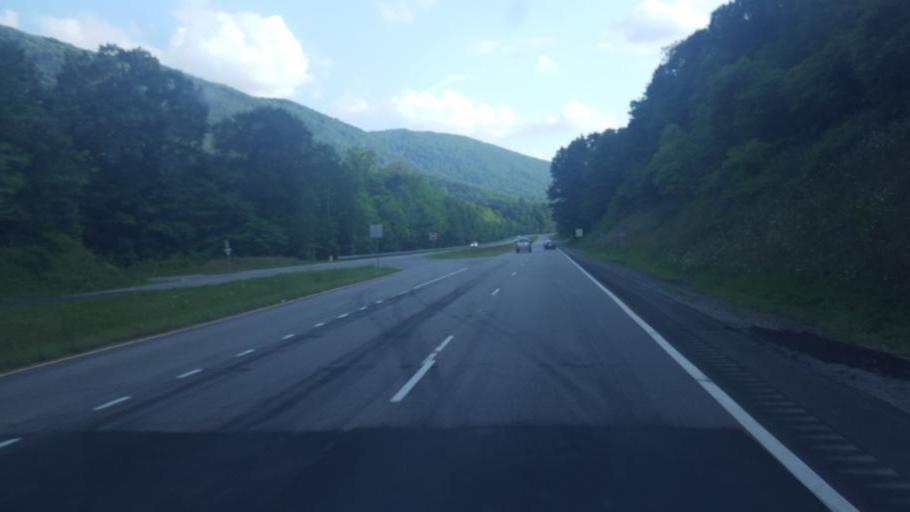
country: US
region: Virginia
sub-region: Wise County
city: Big Stone Gap
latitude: 36.8369
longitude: -82.7659
